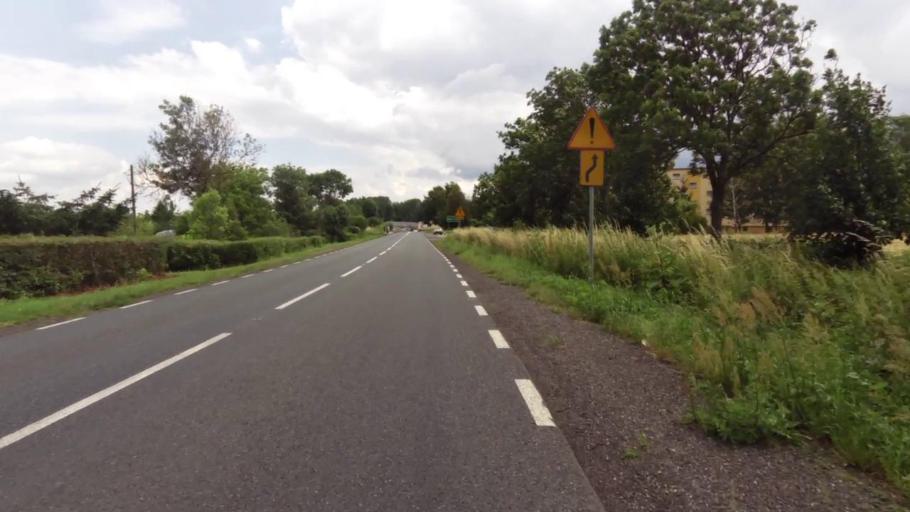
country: PL
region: West Pomeranian Voivodeship
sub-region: Powiat pyrzycki
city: Lipiany
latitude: 52.9953
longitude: 15.0493
